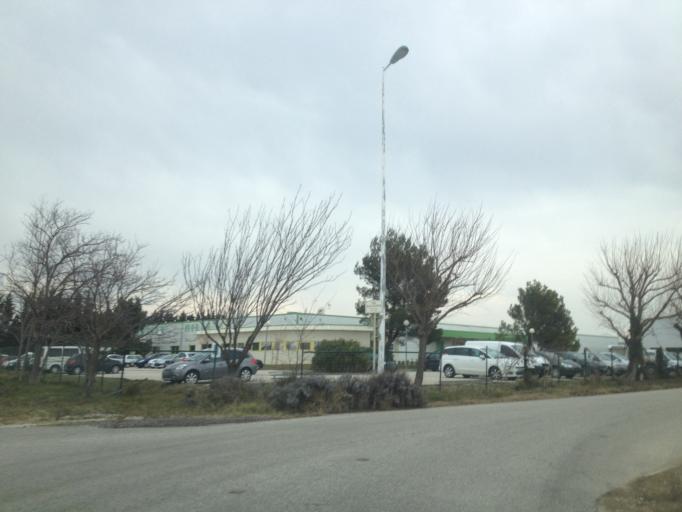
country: FR
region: Provence-Alpes-Cote d'Azur
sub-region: Departement du Vaucluse
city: Courthezon
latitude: 44.1026
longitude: 4.8866
